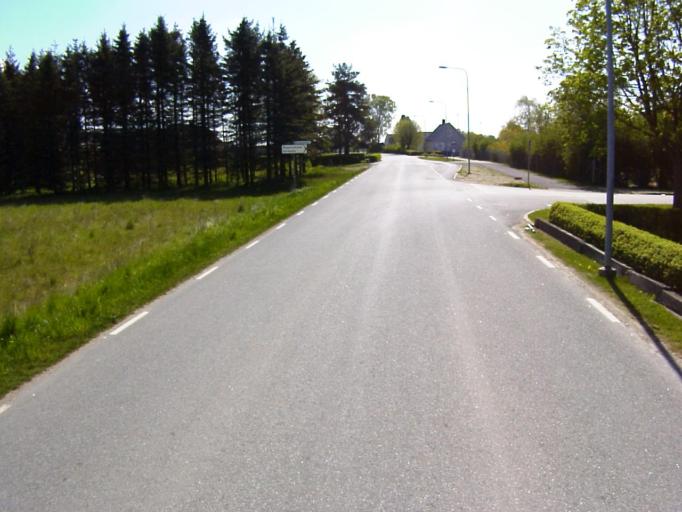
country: SE
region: Skane
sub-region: Kristianstads Kommun
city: Fjalkinge
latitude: 56.0189
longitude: 14.2232
